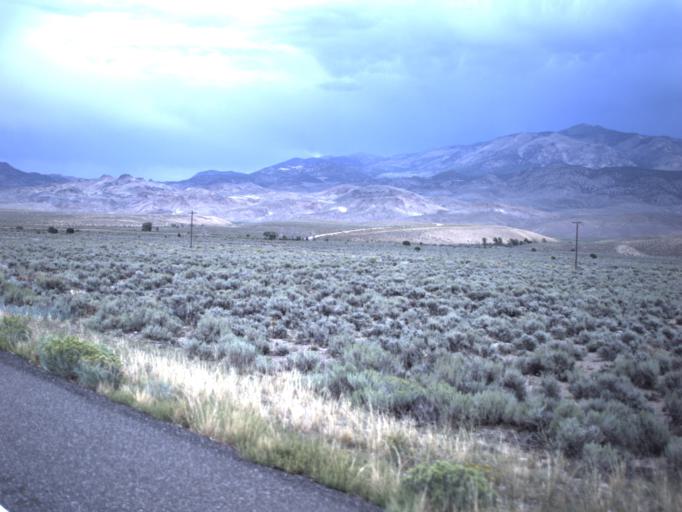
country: US
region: Utah
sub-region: Piute County
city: Junction
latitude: 38.3959
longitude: -112.2310
